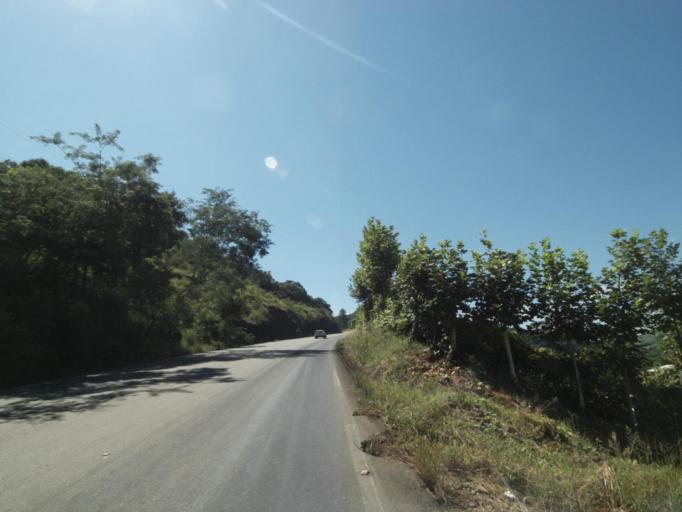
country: BR
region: Rio Grande do Sul
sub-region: Bento Goncalves
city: Bento Goncalves
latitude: -29.1006
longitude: -51.6248
